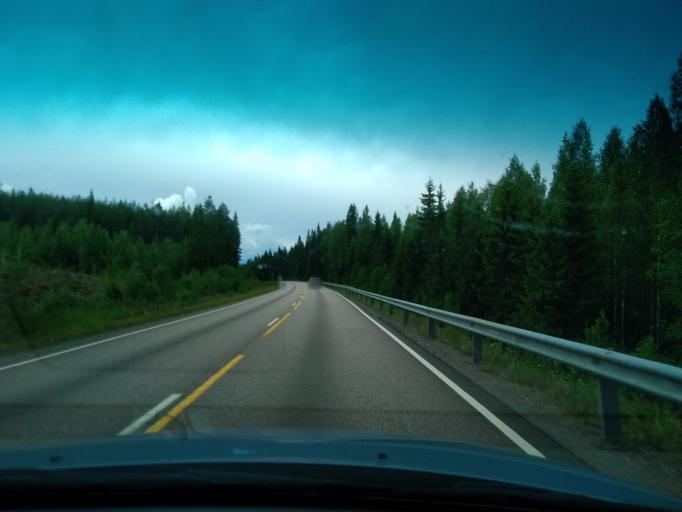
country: FI
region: Central Finland
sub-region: Keuruu
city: Multia
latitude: 62.3748
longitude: 24.7422
